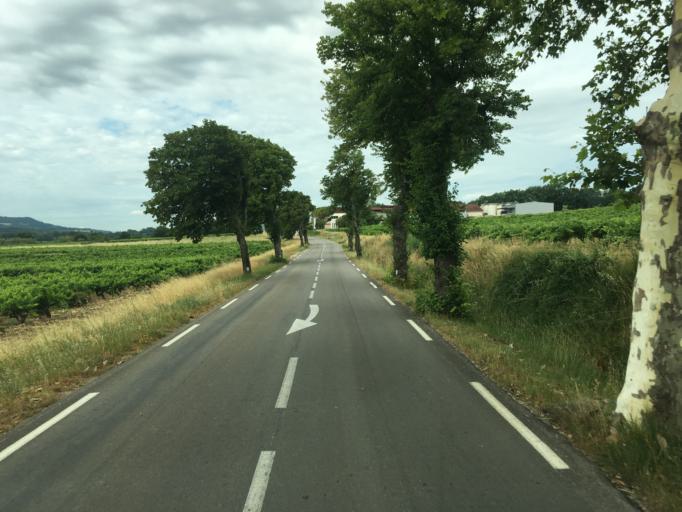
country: FR
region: Provence-Alpes-Cote d'Azur
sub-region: Departement du Vaucluse
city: Visan
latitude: 44.2969
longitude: 5.0055
